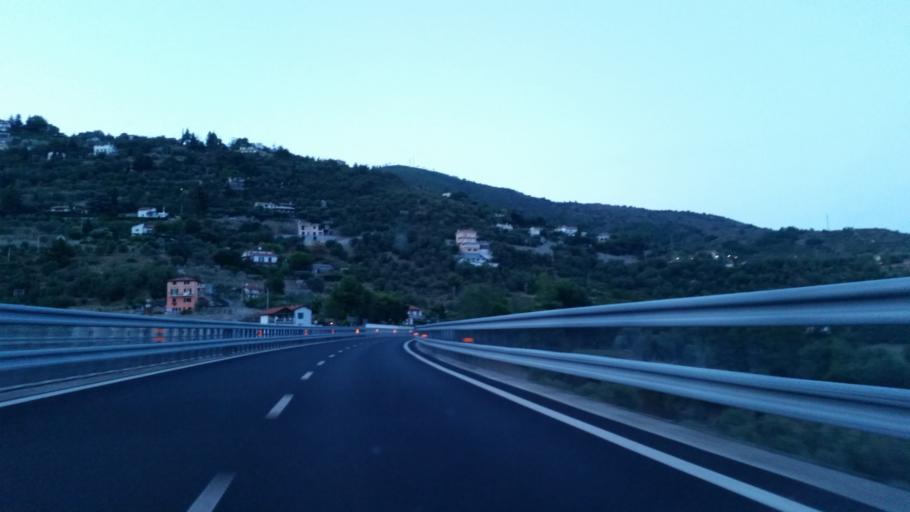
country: IT
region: Liguria
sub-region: Provincia di Imperia
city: San Remo
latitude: 43.8368
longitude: 7.7456
